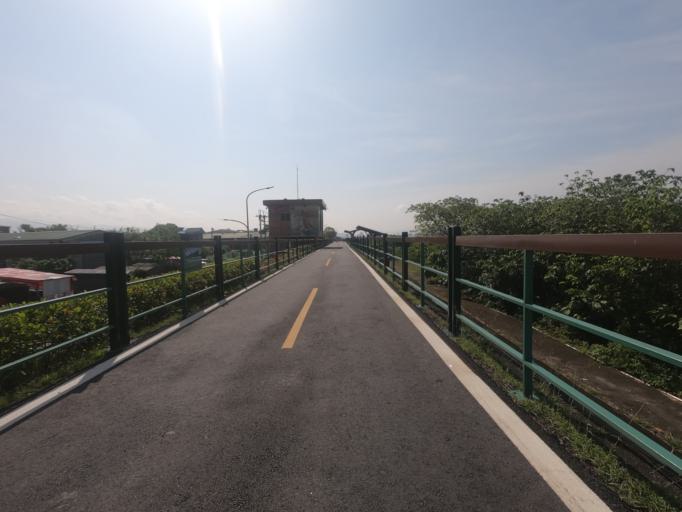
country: TW
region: Taipei
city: Taipei
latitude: 25.1072
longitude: 121.4701
